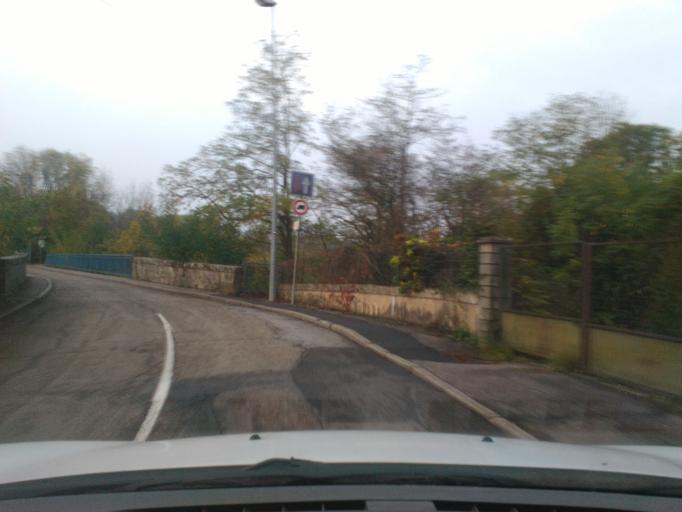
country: FR
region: Lorraine
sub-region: Departement des Vosges
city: Mirecourt
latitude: 48.3046
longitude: 6.1278
